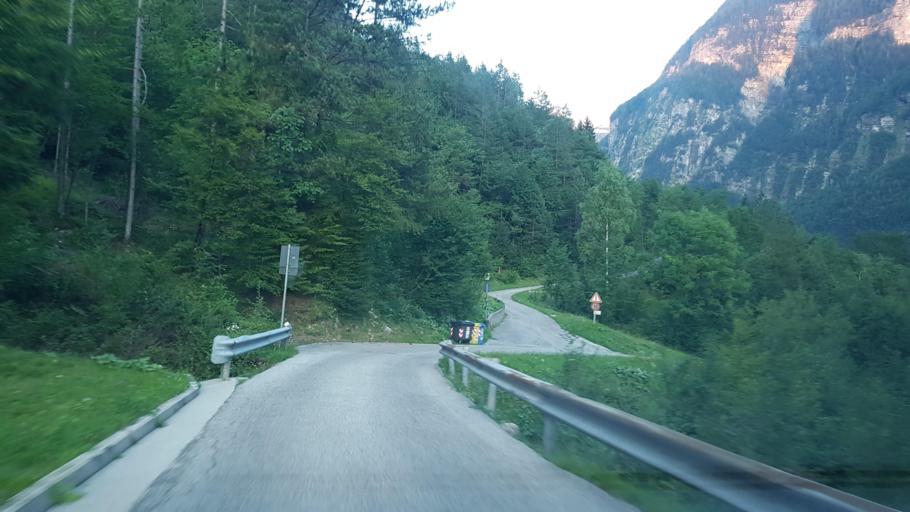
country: IT
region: Friuli Venezia Giulia
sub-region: Provincia di Udine
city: Malborghetto
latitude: 46.4006
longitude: 13.4271
